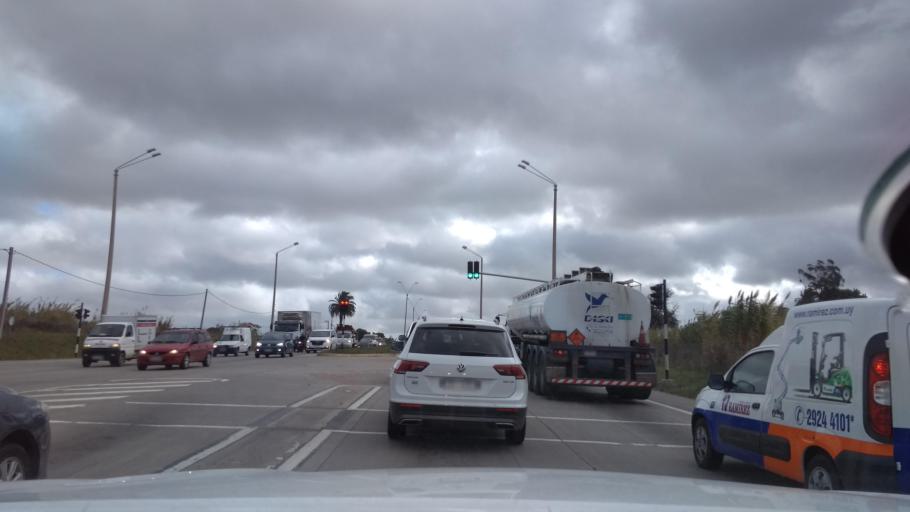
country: UY
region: Canelones
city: Toledo
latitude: -34.7940
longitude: -56.1226
